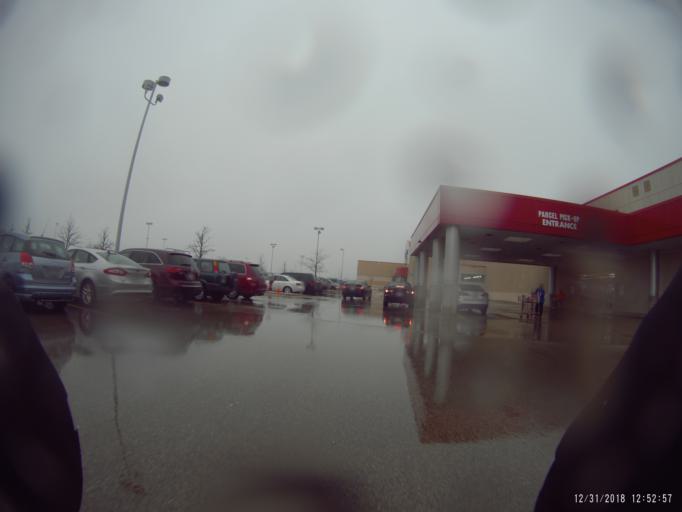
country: US
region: Wisconsin
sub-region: Dane County
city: Middleton
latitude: 43.0493
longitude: -89.5013
